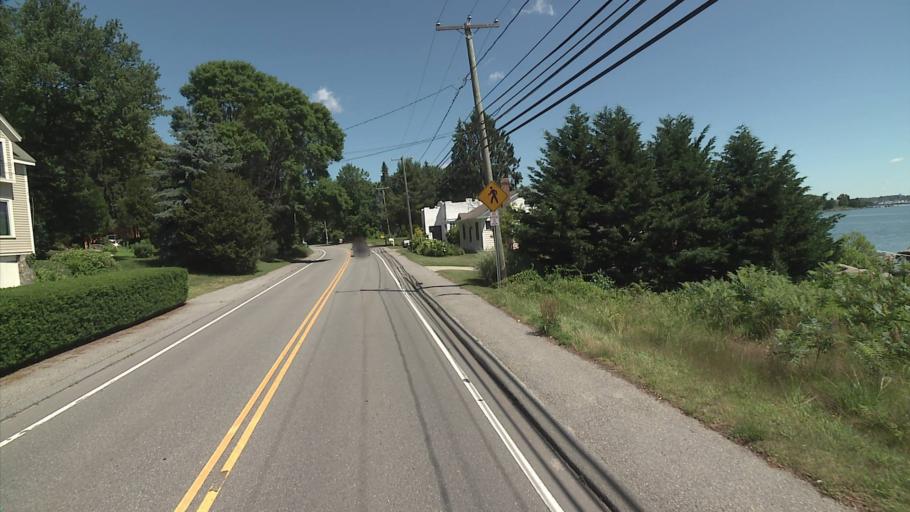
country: US
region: Connecticut
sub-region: New London County
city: Noank
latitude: 41.3300
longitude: -71.9911
